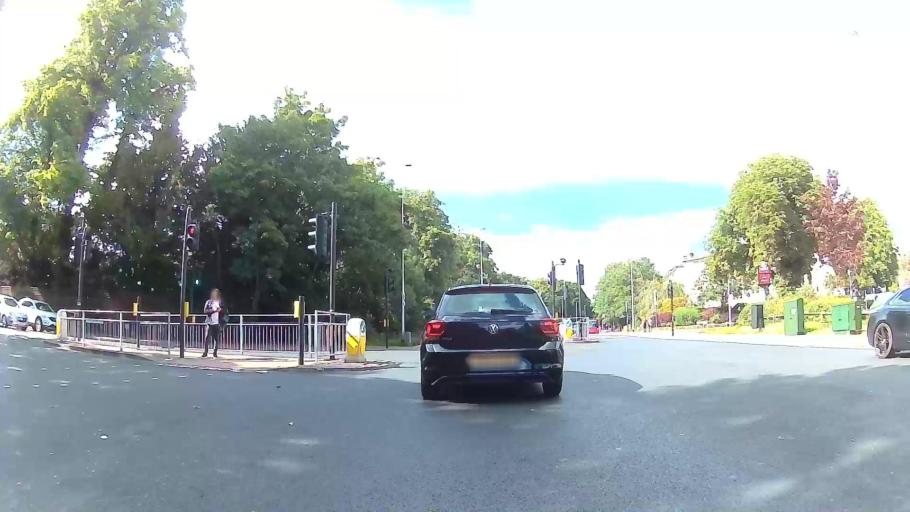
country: GB
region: England
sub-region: Greater London
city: Woodford Green
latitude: 51.5831
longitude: 0.0202
